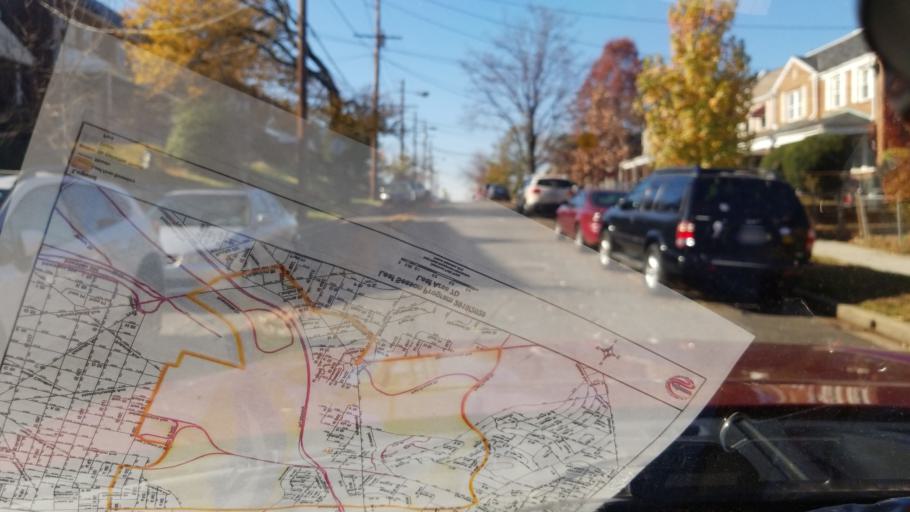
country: US
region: Maryland
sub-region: Prince George's County
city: Capitol Heights
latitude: 38.8919
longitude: -76.9489
